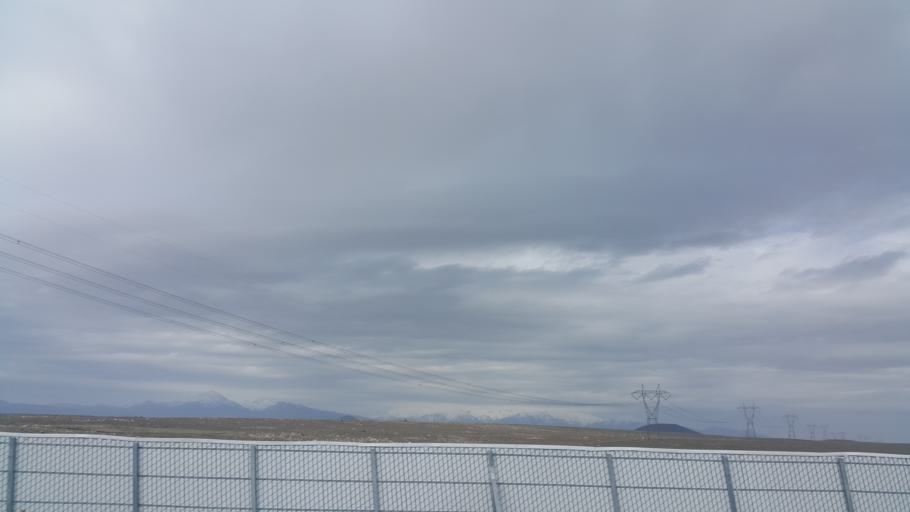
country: TR
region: Nigde
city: Altunhisar
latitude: 37.8984
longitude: 34.1333
